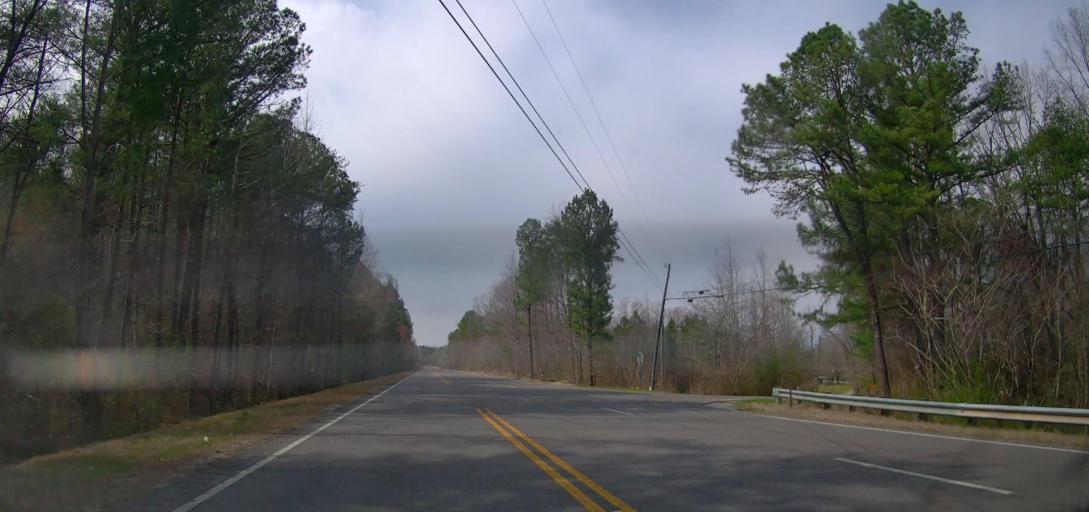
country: US
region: Alabama
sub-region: Walker County
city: Carbon Hill
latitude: 33.9104
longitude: -87.5587
